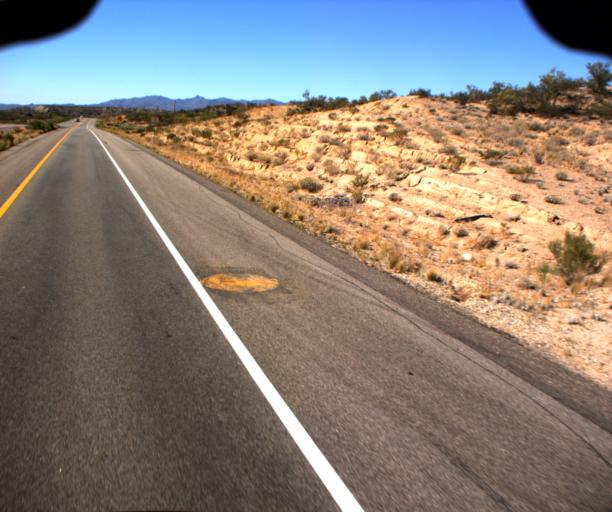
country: US
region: Arizona
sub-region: Yavapai County
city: Bagdad
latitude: 34.8139
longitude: -113.6263
